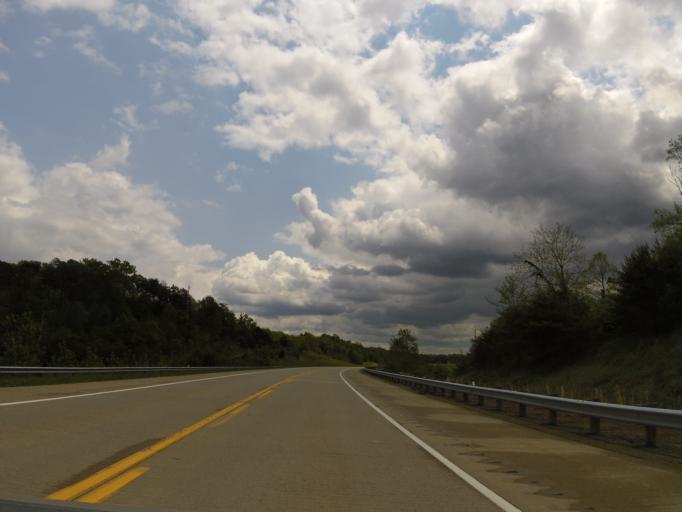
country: US
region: West Virginia
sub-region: Mason County
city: New Haven
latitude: 38.9967
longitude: -81.8728
